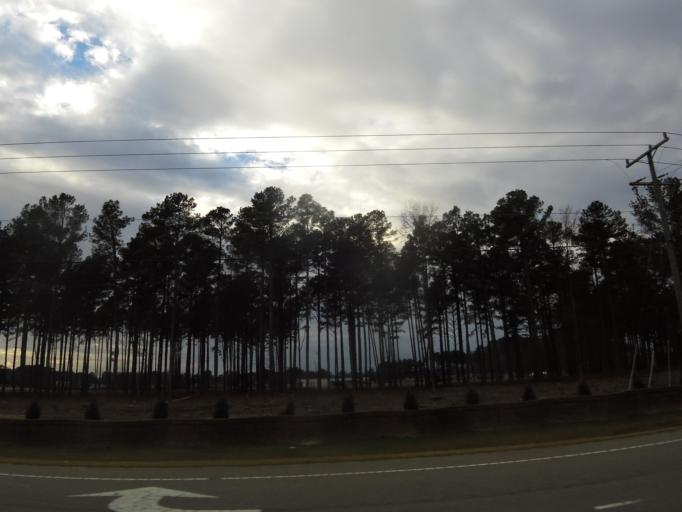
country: US
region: North Carolina
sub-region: Nash County
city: Rocky Mount
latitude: 36.0131
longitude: -77.7721
